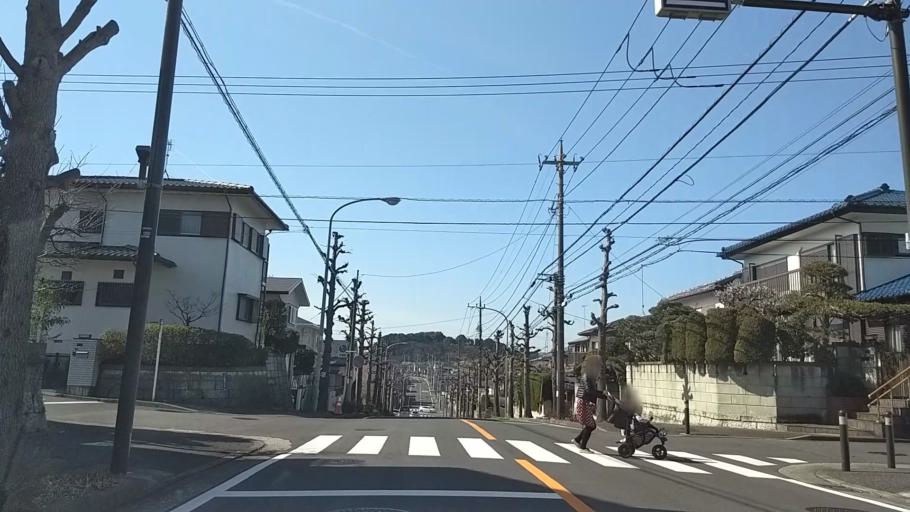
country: JP
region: Kanagawa
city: Kamakura
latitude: 35.3737
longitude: 139.5473
